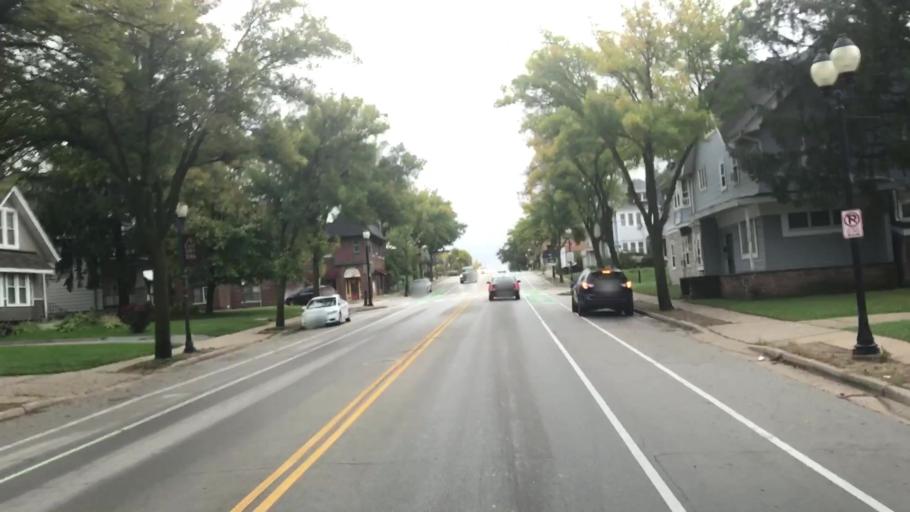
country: US
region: Wisconsin
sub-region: Milwaukee County
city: Wauwatosa
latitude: 43.0607
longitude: -87.9918
